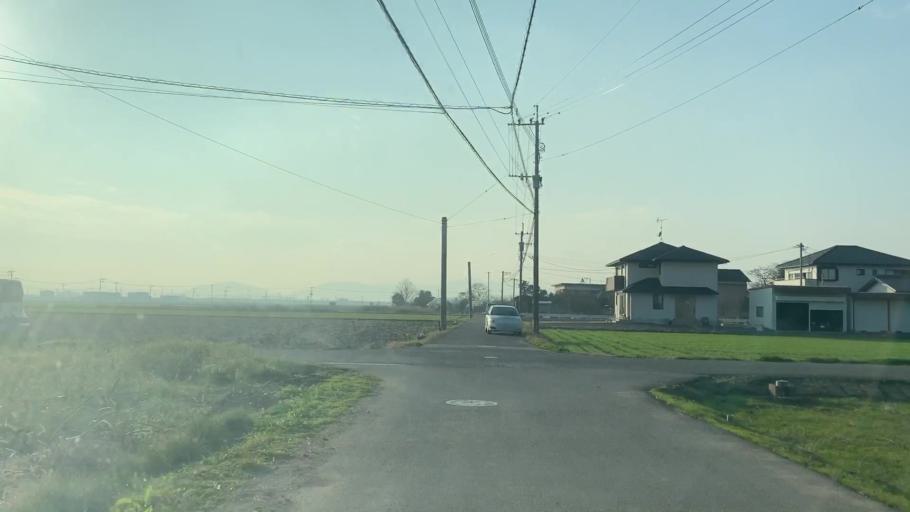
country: JP
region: Saga Prefecture
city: Saga-shi
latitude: 33.2625
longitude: 130.2604
